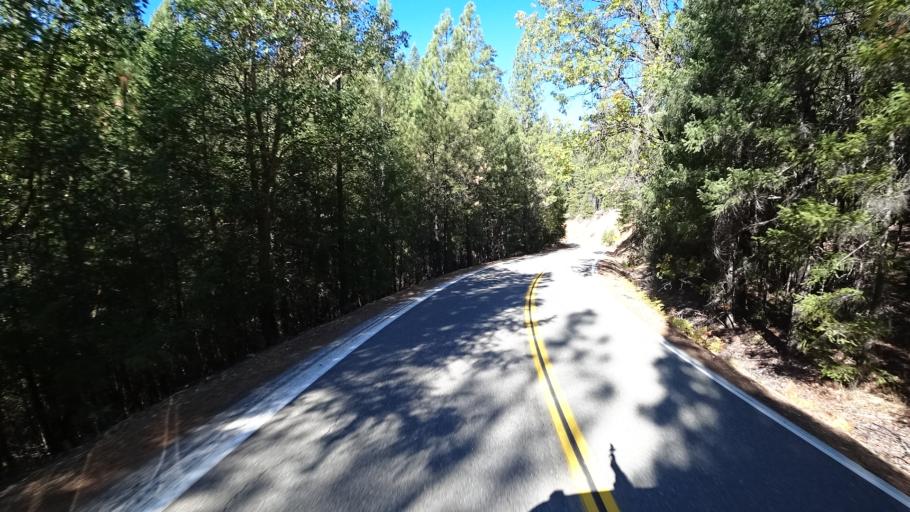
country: US
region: California
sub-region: Trinity County
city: Weaverville
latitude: 41.2026
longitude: -123.0696
